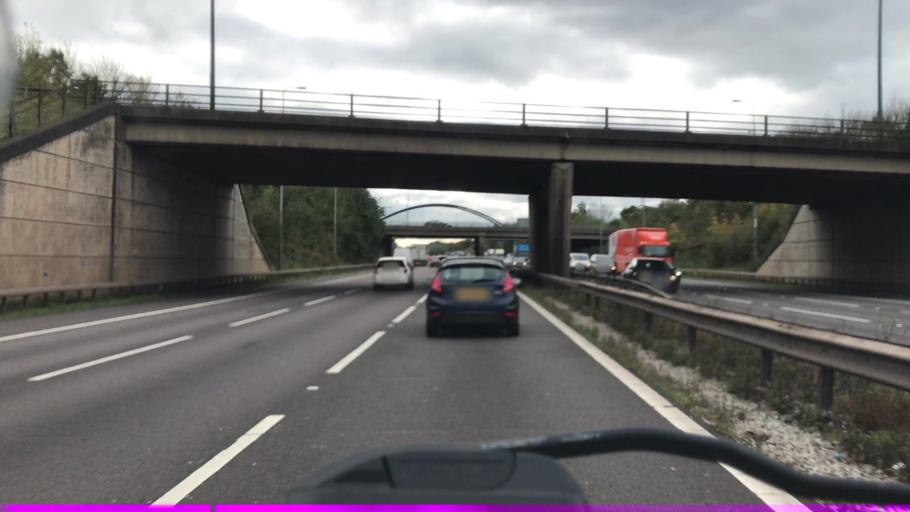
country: GB
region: England
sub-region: Solihull
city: Cheswick Green
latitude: 52.3806
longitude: -1.7858
